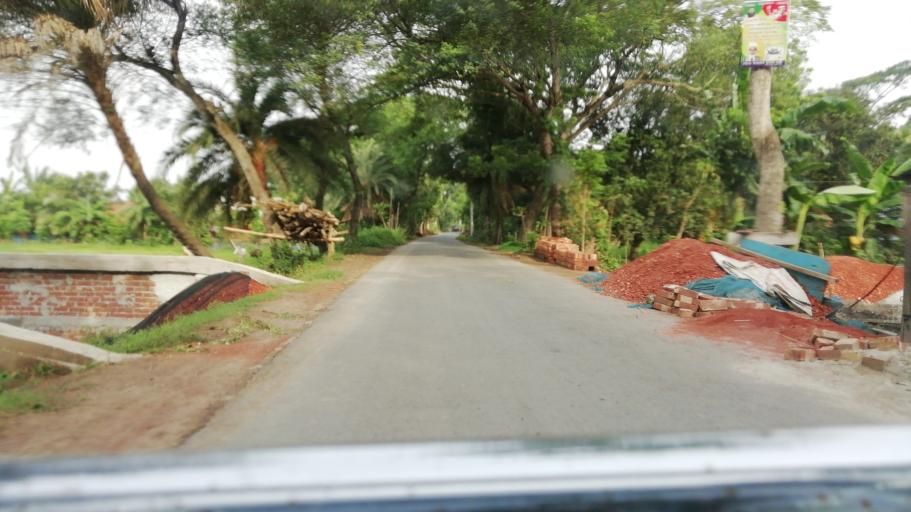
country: BD
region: Khulna
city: Kesabpur
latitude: 23.0353
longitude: 89.2922
